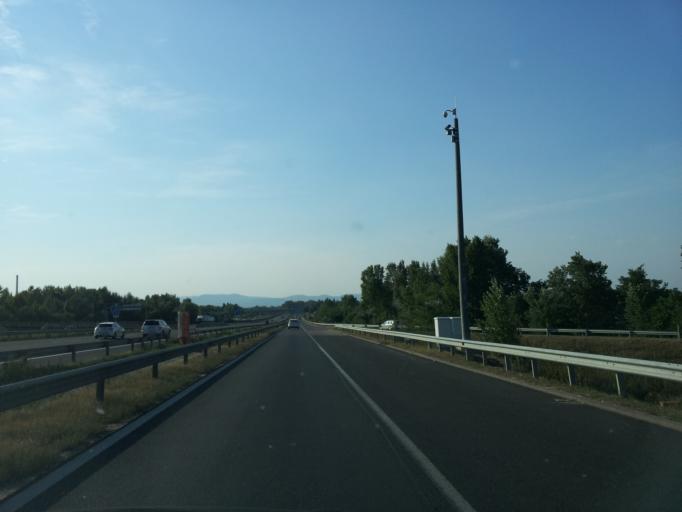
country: HU
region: Budapest
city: Budapest XV. keruelet
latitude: 47.5748
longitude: 19.1574
